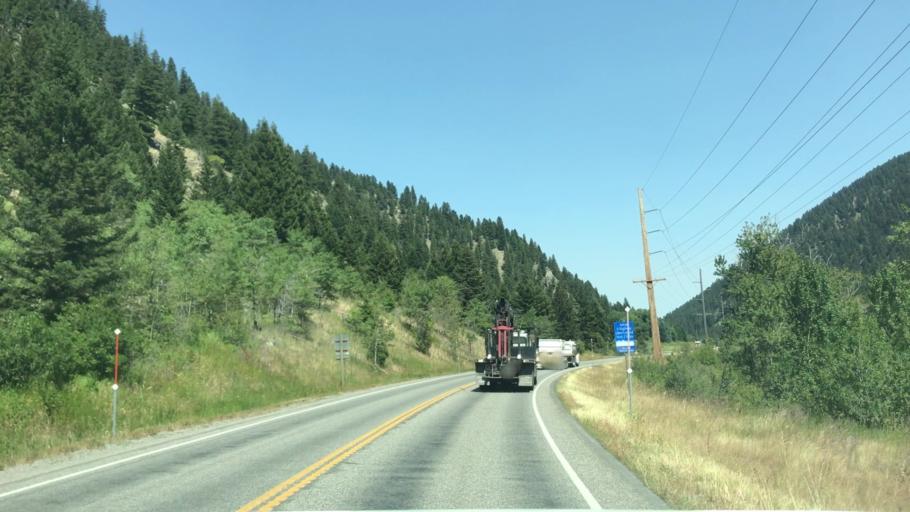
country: US
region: Montana
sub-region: Gallatin County
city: Four Corners
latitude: 45.5046
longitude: -111.2669
